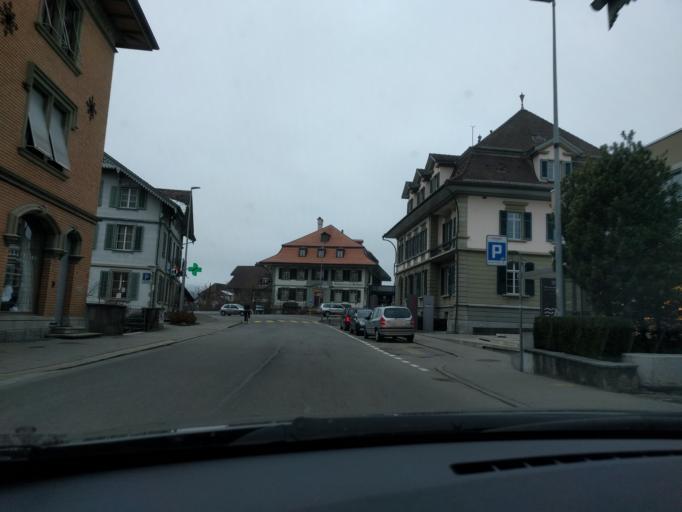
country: CH
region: Bern
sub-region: Emmental District
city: Langnau
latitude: 46.9406
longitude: 7.7841
